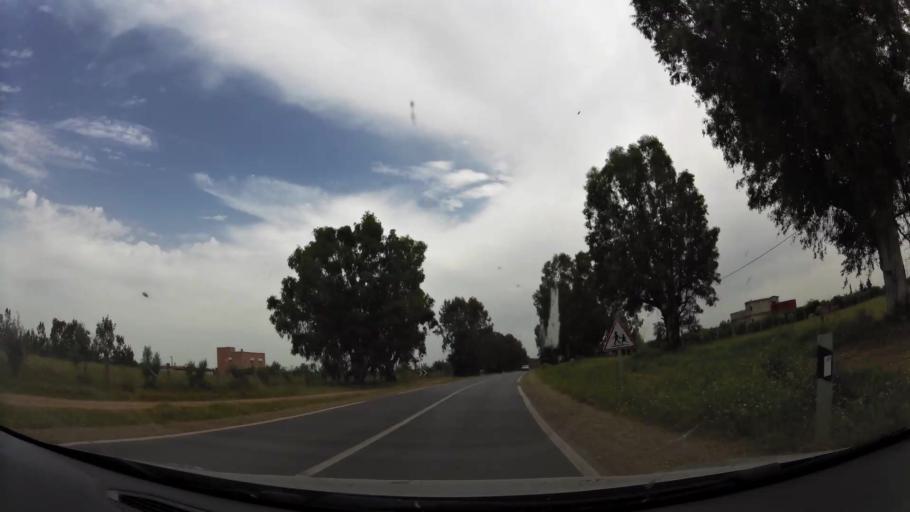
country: MA
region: Rabat-Sale-Zemmour-Zaer
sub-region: Khemisset
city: Tiflet
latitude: 33.8525
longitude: -6.2682
